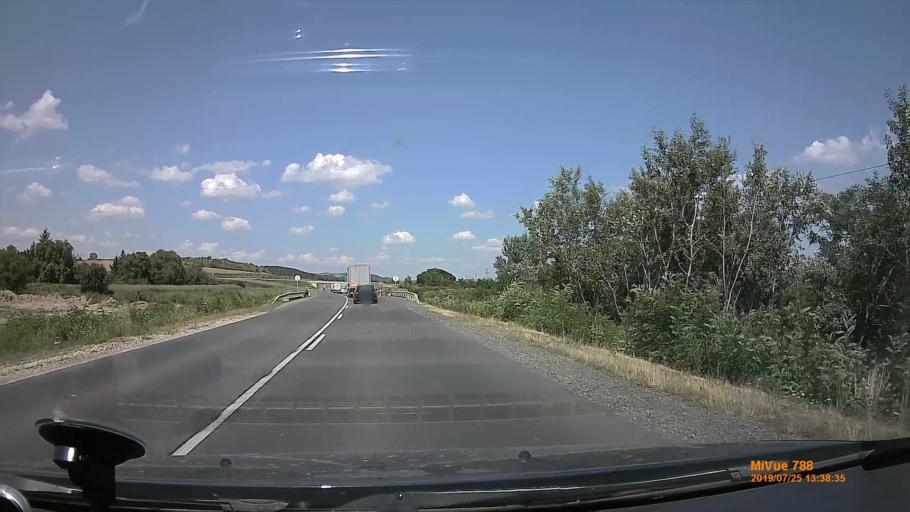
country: HU
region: Borsod-Abauj-Zemplen
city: Encs
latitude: 48.4174
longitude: 21.1787
